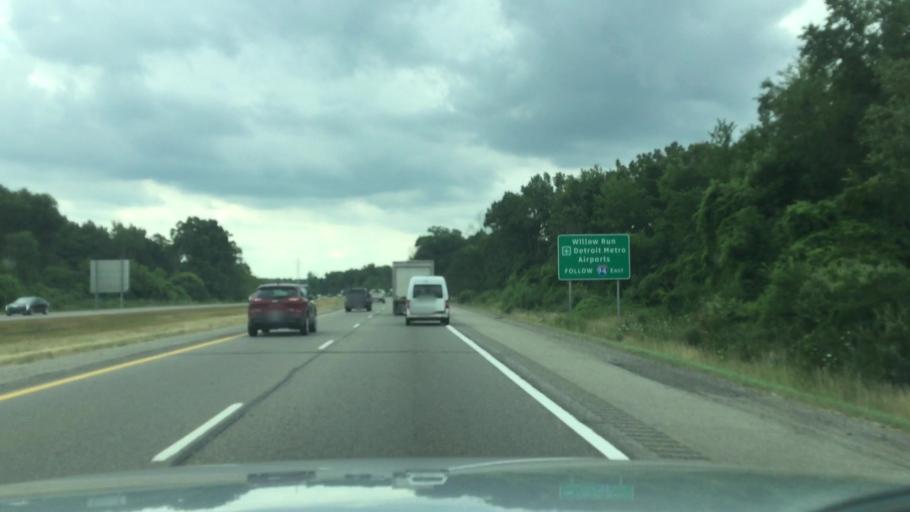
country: US
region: Michigan
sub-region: Washtenaw County
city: Ann Arbor
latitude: 42.2406
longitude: -83.6844
